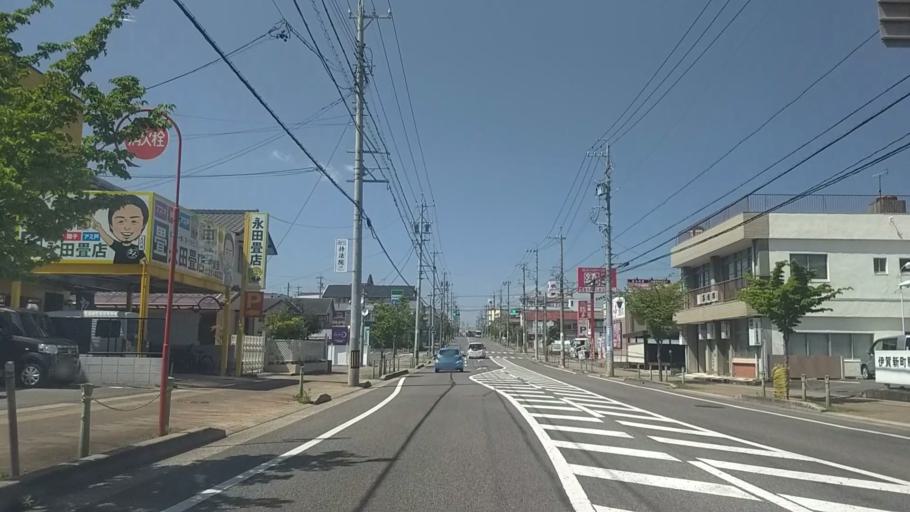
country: JP
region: Aichi
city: Okazaki
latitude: 34.9723
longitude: 137.1705
